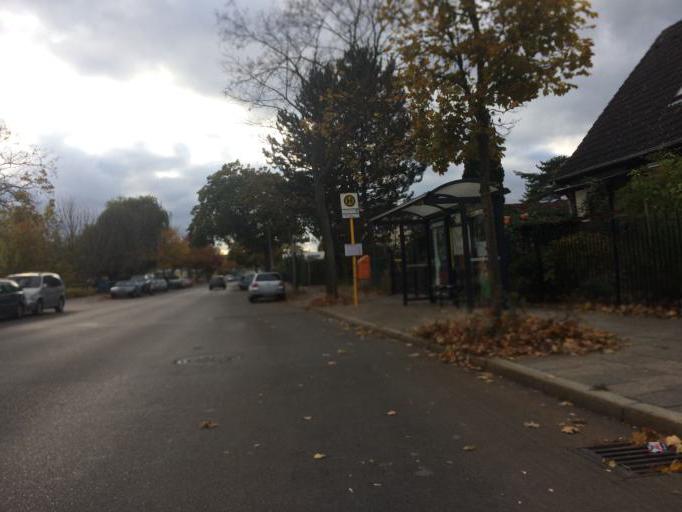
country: DE
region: Berlin
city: Lubars
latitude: 52.6060
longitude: 13.3393
